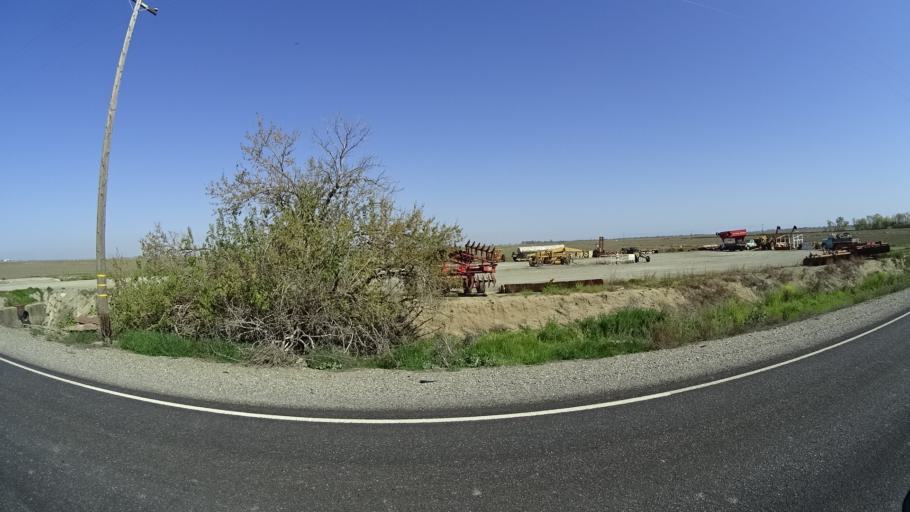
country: US
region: California
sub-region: Glenn County
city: Willows
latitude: 39.4578
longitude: -122.0480
